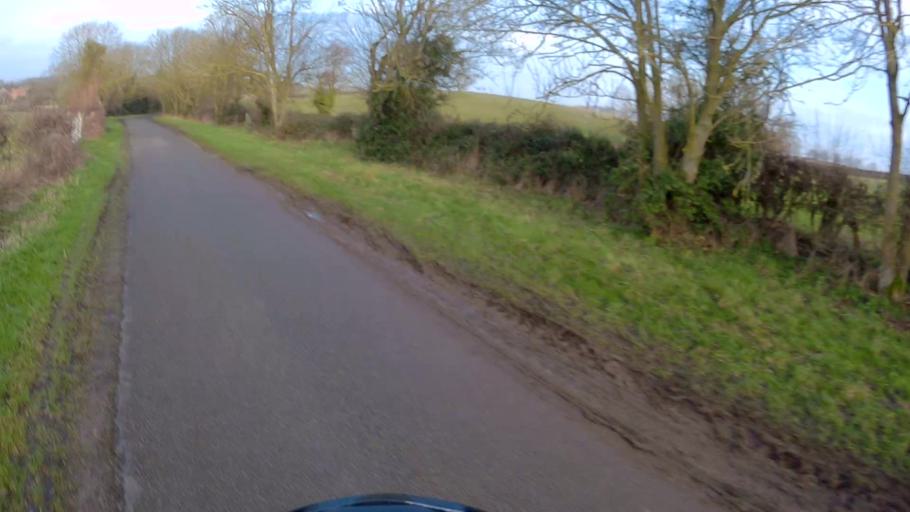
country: GB
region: England
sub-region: Lincolnshire
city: Bourne
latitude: 52.7456
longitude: -0.4182
